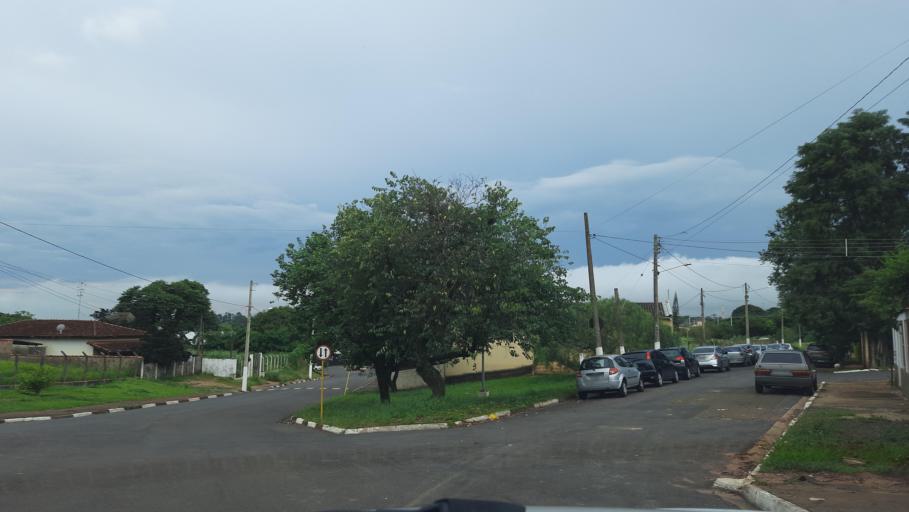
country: BR
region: Sao Paulo
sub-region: Casa Branca
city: Casa Branca
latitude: -21.7818
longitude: -47.0726
